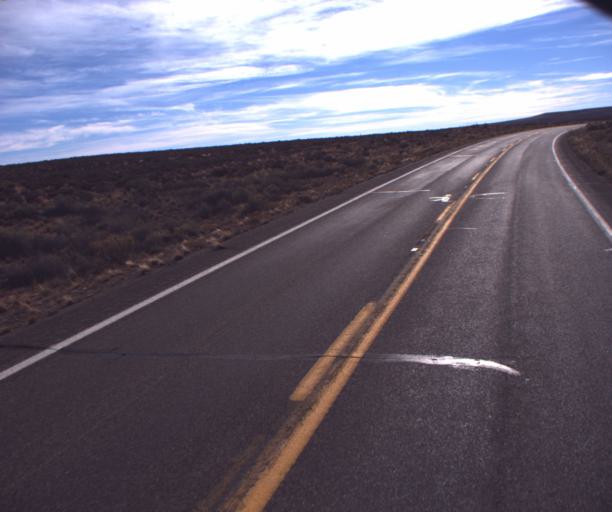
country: US
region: Arizona
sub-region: Coconino County
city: LeChee
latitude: 36.8289
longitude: -111.3113
